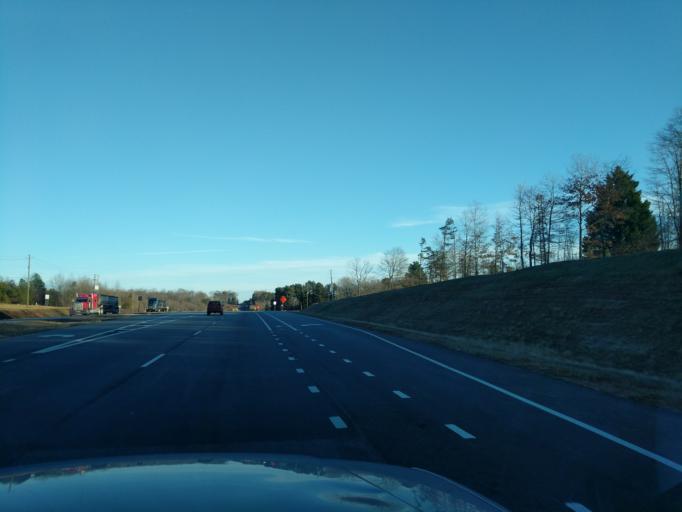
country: US
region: Georgia
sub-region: Stephens County
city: Toccoa
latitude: 34.5226
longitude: -83.2445
